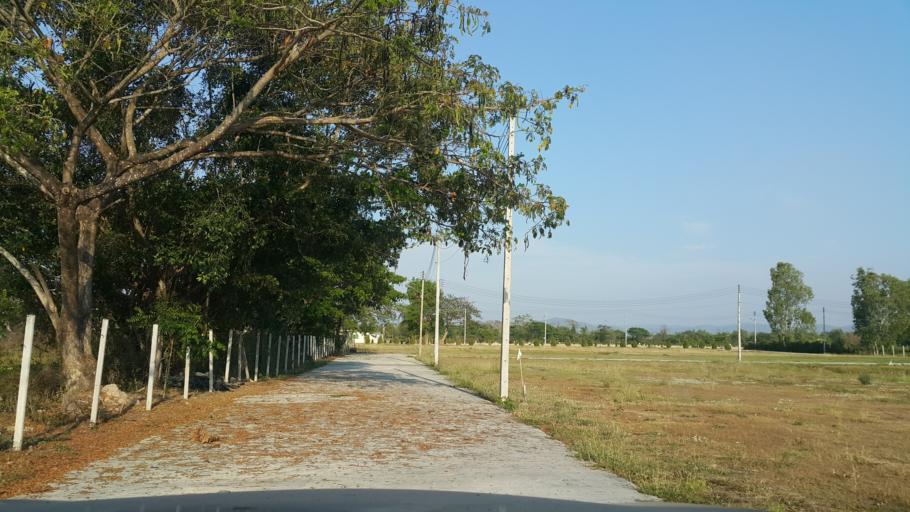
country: TH
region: Chiang Mai
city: San Sai
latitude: 18.8355
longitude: 99.0918
